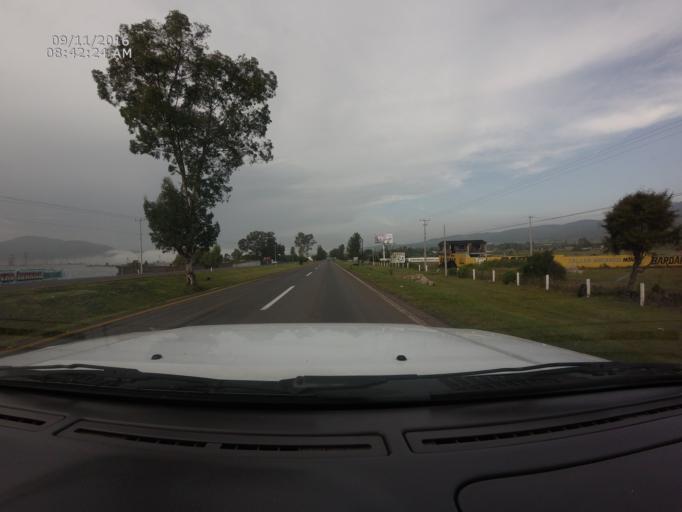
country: MX
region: Michoacan
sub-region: Morelia
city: La Mintzita (Piedra Dura)
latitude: 19.5914
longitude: -101.2990
